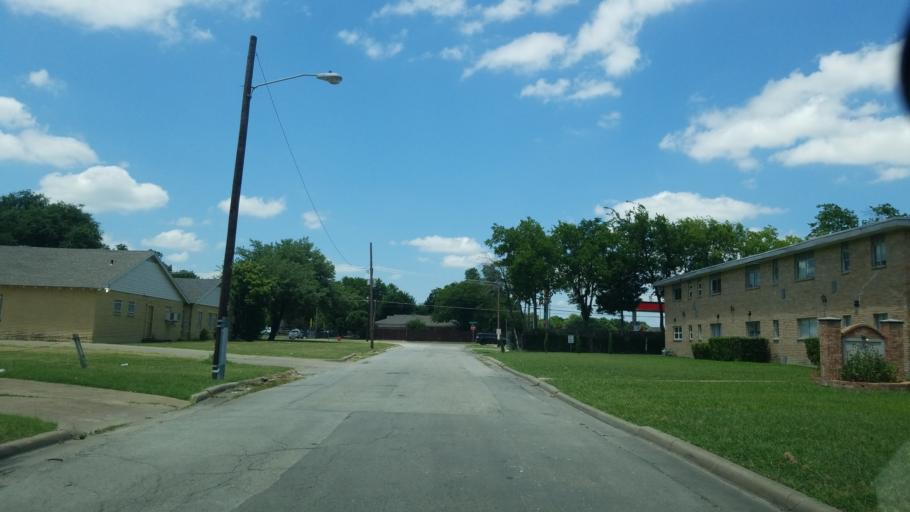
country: US
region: Texas
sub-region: Dallas County
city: Balch Springs
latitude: 32.7334
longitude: -96.7043
